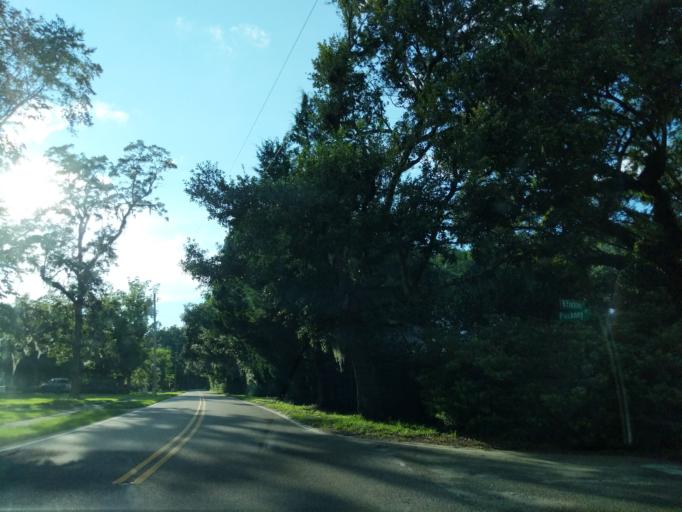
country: US
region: South Carolina
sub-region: Charleston County
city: Awendaw
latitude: 33.0929
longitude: -79.4651
